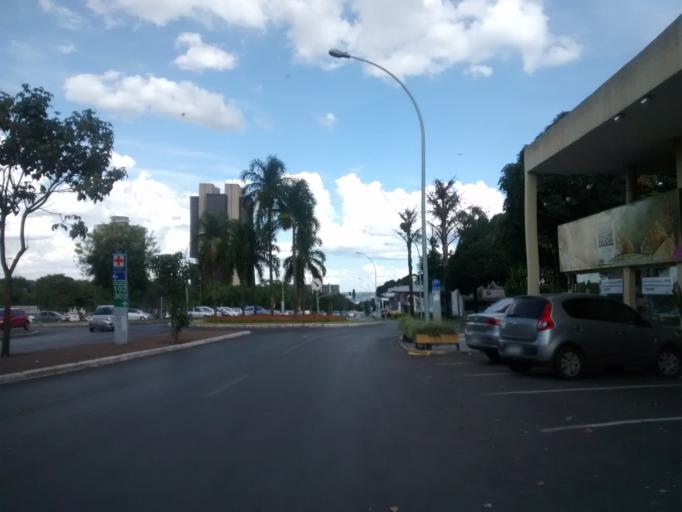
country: BR
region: Federal District
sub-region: Brasilia
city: Brasilia
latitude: -15.8011
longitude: -47.8906
